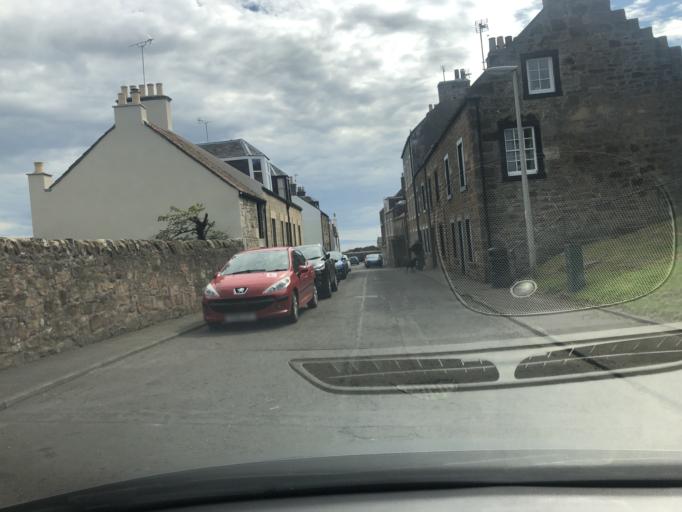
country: GB
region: Scotland
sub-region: Fife
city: Anstruther
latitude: 56.2266
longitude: -2.6822
